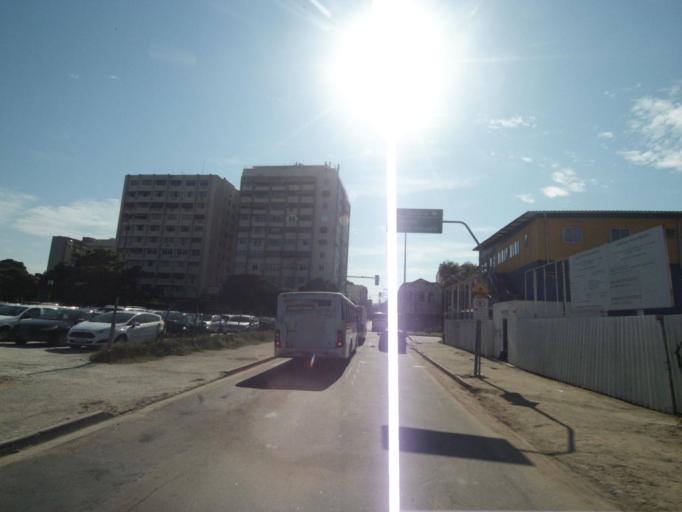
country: BR
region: Rio de Janeiro
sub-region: Niteroi
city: Niteroi
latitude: -22.8878
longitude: -43.1253
